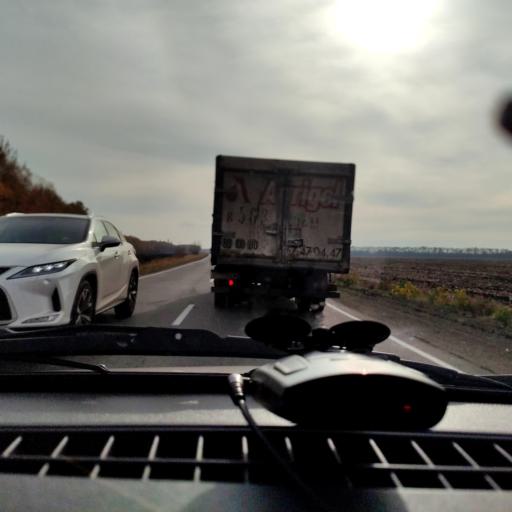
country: RU
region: Voronezj
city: Shilovo
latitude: 51.4412
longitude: 38.9966
